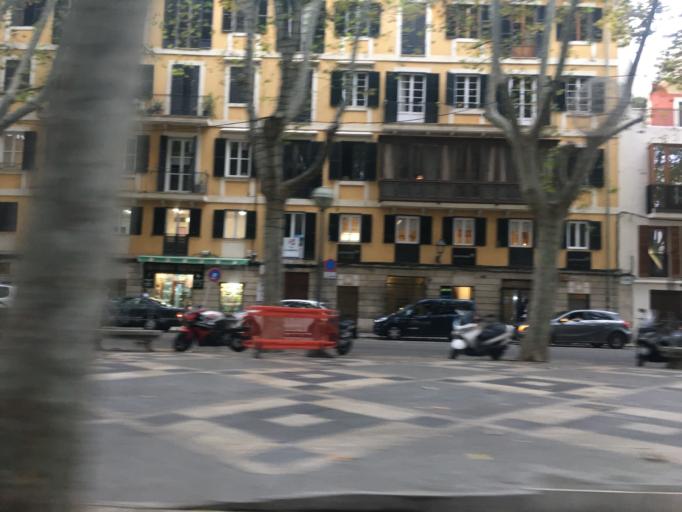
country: ES
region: Balearic Islands
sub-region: Illes Balears
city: Palma
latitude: 39.5727
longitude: 2.6504
